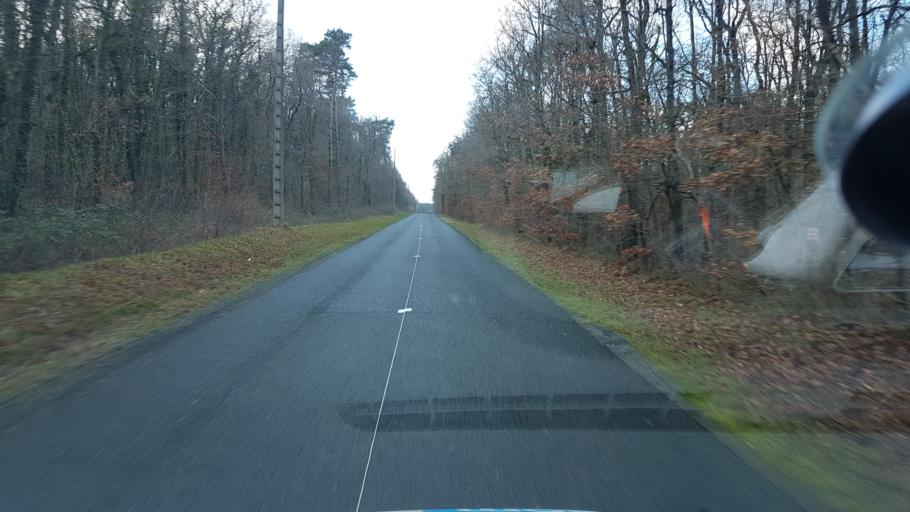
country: FR
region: Ile-de-France
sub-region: Departement de Seine-et-Marne
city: Montigny-sur-Loing
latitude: 48.2756
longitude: 2.7745
